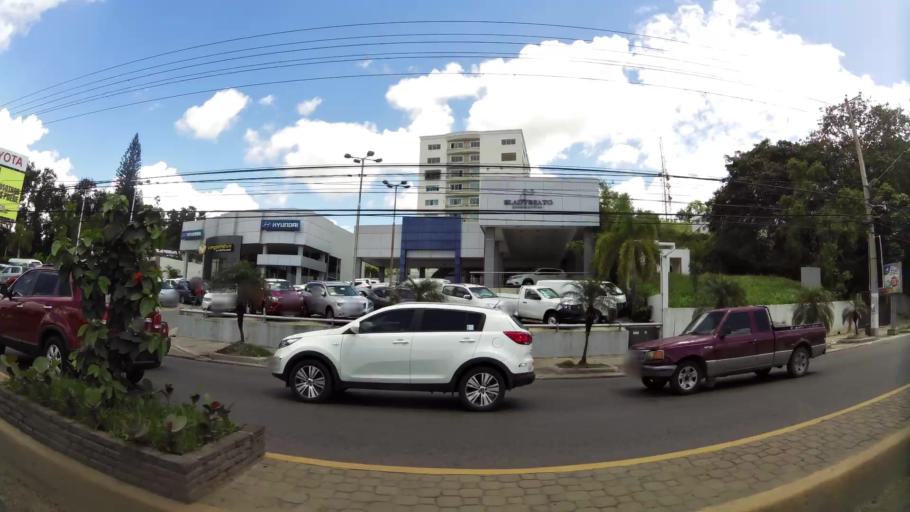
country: DO
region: Santiago
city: Santiago de los Caballeros
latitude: 19.4662
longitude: -70.6866
